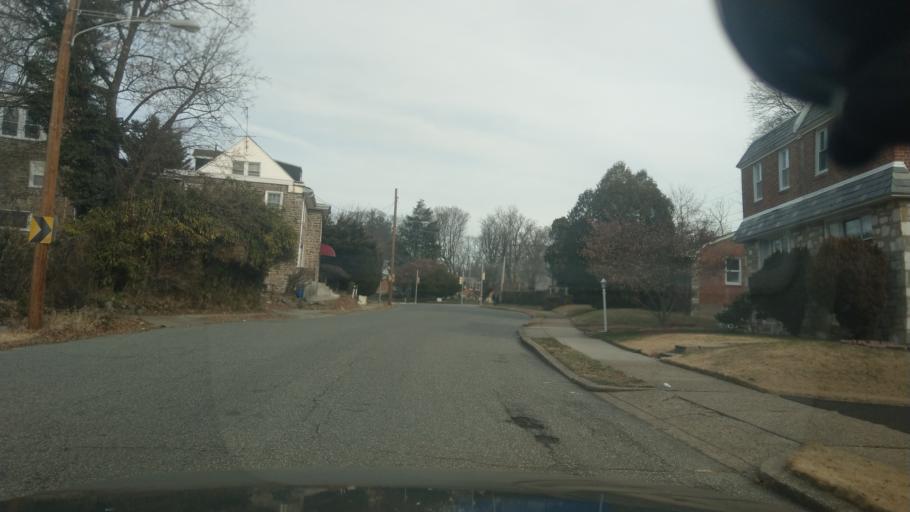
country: US
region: Pennsylvania
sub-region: Montgomery County
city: Wyncote
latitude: 40.0519
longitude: -75.1345
